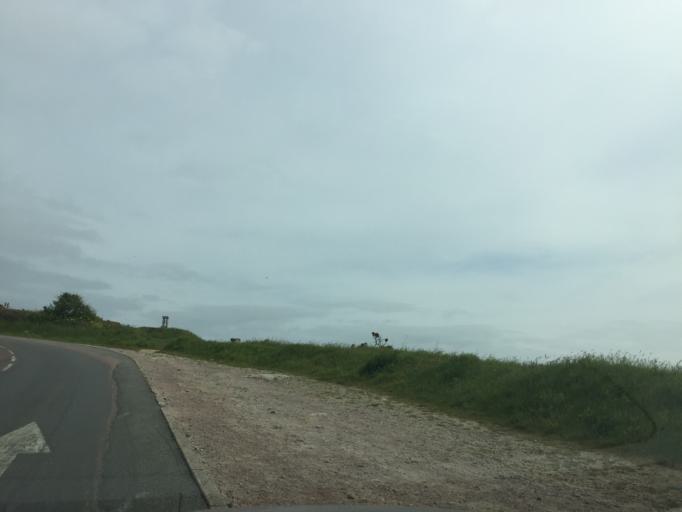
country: FR
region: Brittany
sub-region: Departement des Cotes-d'Armor
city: Saint-Cast-le-Guildo
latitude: 48.6434
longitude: -2.2452
